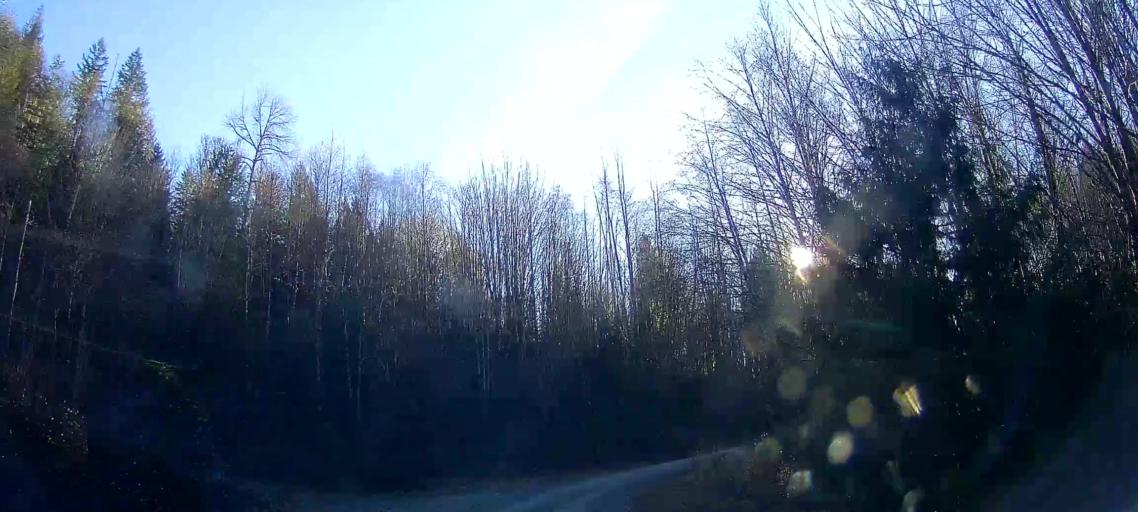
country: US
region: Washington
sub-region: Snohomish County
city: Darrington
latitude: 48.5507
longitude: -121.7259
